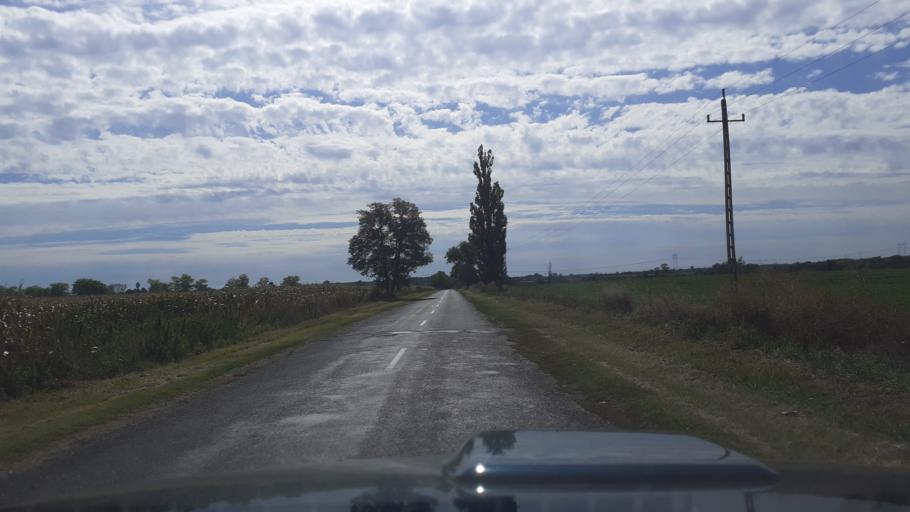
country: HU
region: Fejer
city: Pusztaszabolcs
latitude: 47.1210
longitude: 18.7767
